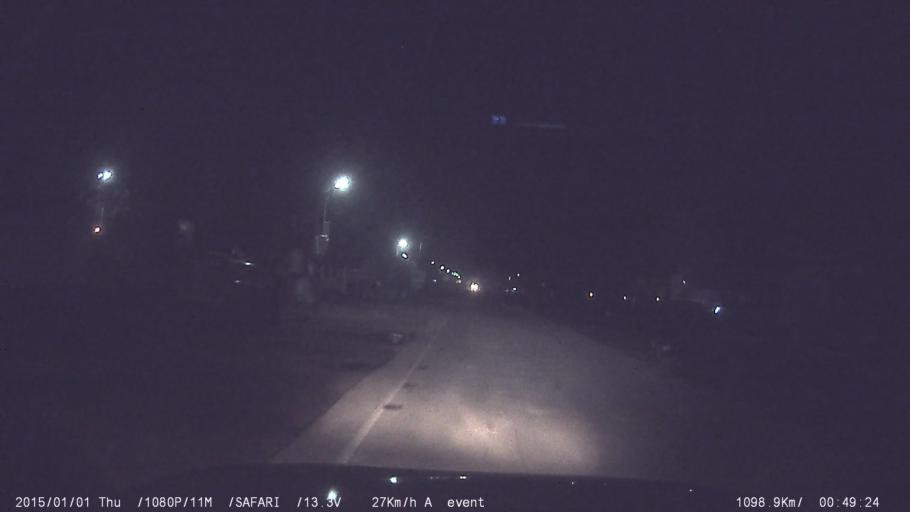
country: IN
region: Tamil Nadu
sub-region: Kancheepuram
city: Singapperumalkovil
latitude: 12.8018
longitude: 80.0253
